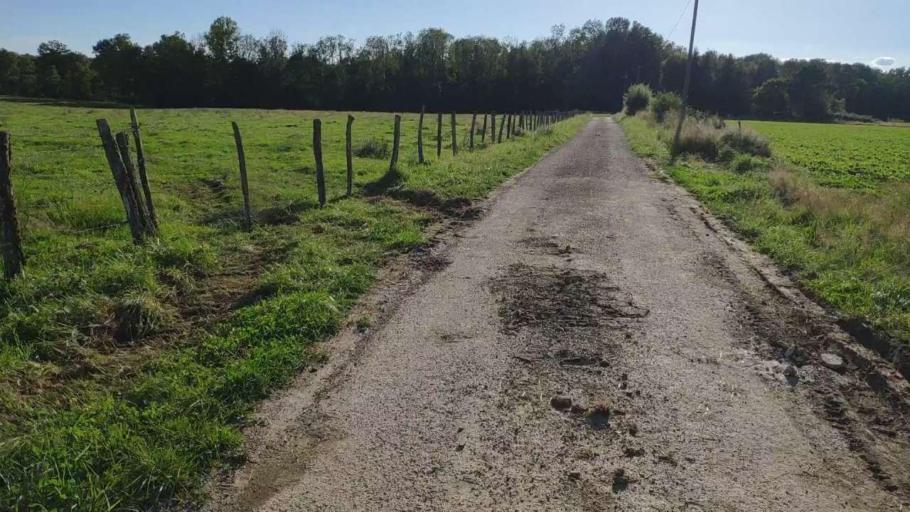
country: FR
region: Franche-Comte
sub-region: Departement du Jura
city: Bletterans
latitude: 46.7819
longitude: 5.4785
